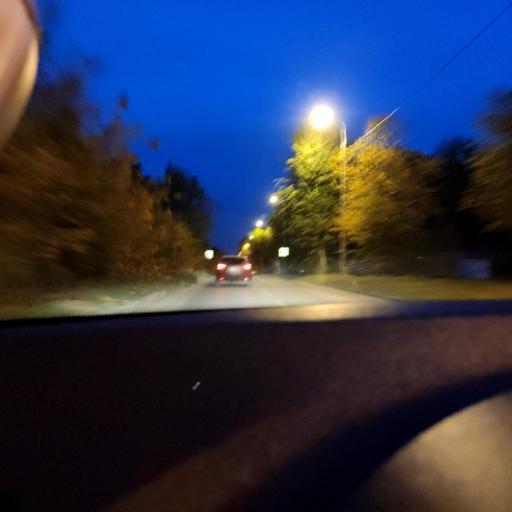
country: RU
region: Samara
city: Samara
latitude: 53.2450
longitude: 50.2570
